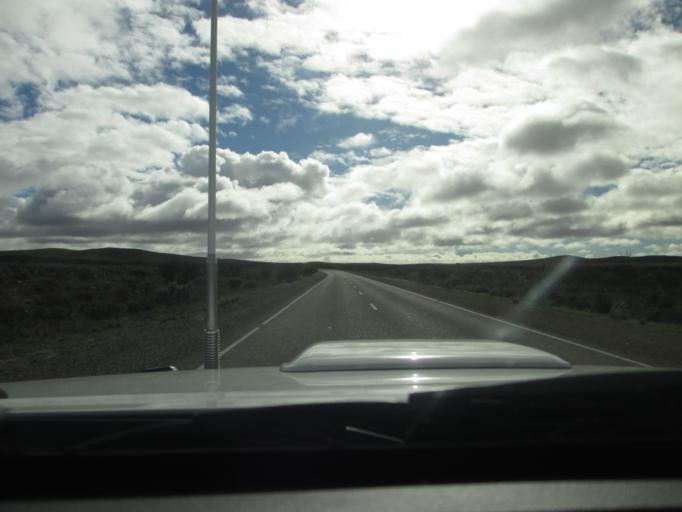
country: AU
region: South Australia
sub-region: Flinders Ranges
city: Quorn
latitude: -32.2003
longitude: 138.5308
